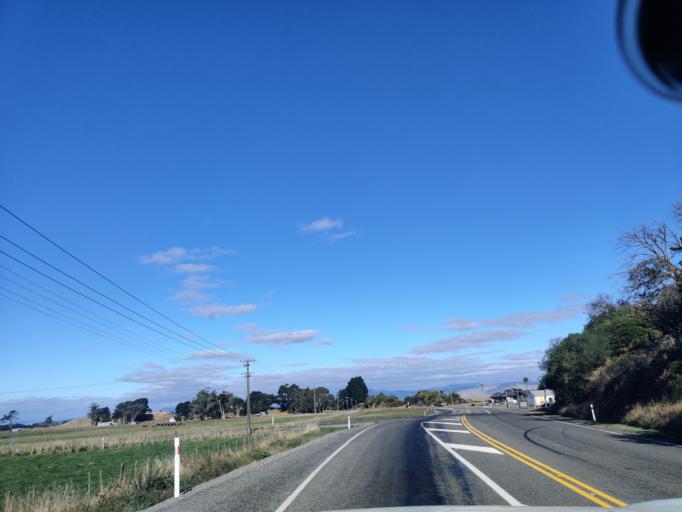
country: NZ
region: Manawatu-Wanganui
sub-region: Horowhenua District
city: Foxton
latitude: -40.4076
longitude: 175.3764
